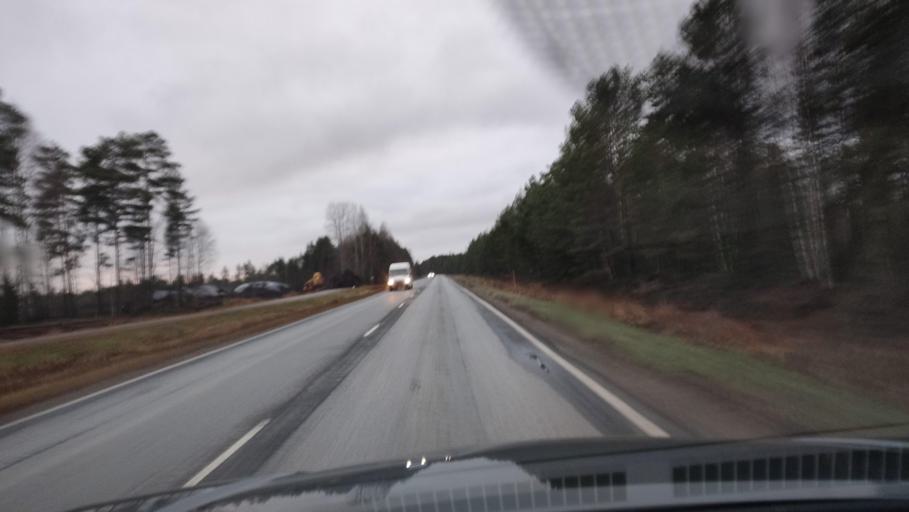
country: FI
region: Southern Ostrobothnia
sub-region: Suupohja
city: Kauhajoki
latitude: 62.3818
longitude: 22.1153
